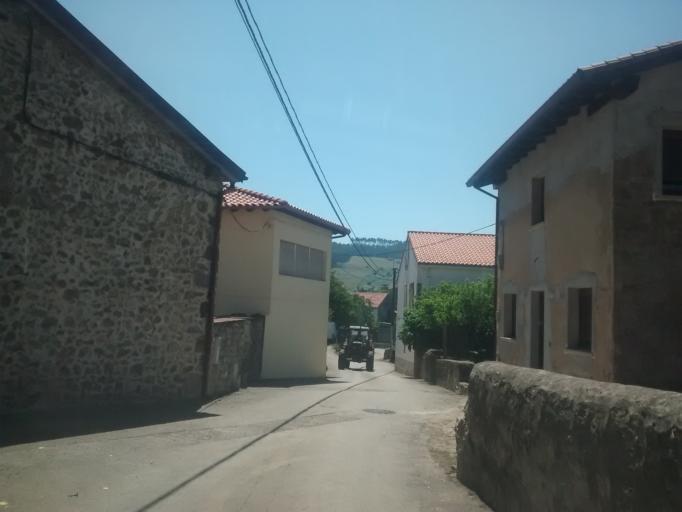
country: ES
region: Cantabria
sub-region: Provincia de Cantabria
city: Arnuero
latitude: 43.4755
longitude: -3.5649
